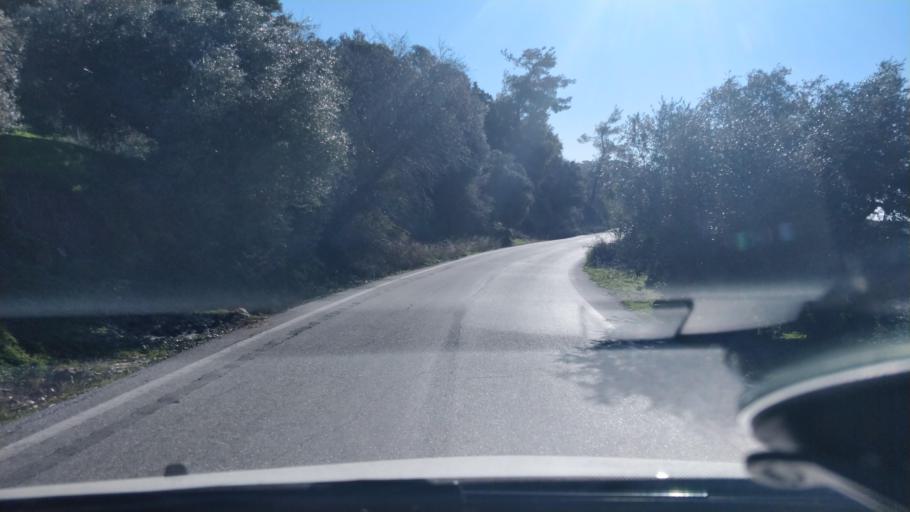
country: GR
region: Crete
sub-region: Nomos Lasithiou
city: Kritsa
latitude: 35.0786
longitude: 25.5975
